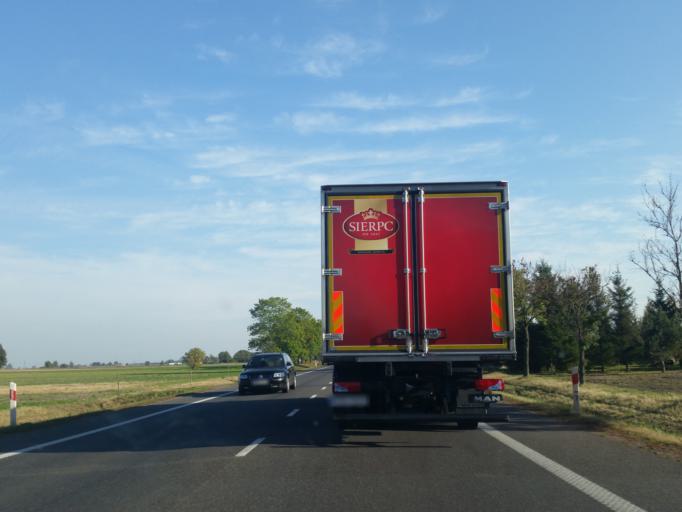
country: PL
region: Masovian Voivodeship
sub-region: Powiat sierpecki
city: Rosciszewo
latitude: 52.8276
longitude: 19.7591
